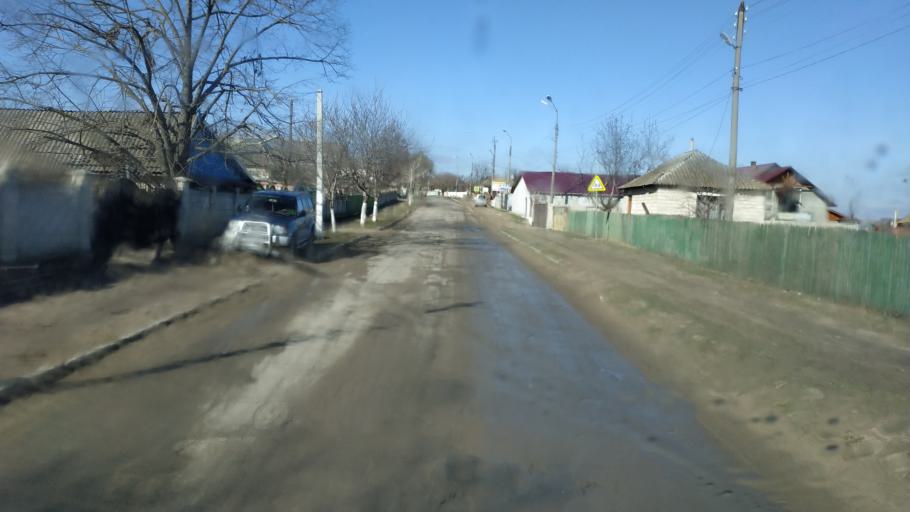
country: MD
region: Hincesti
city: Hincesti
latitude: 46.9710
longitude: 28.5862
